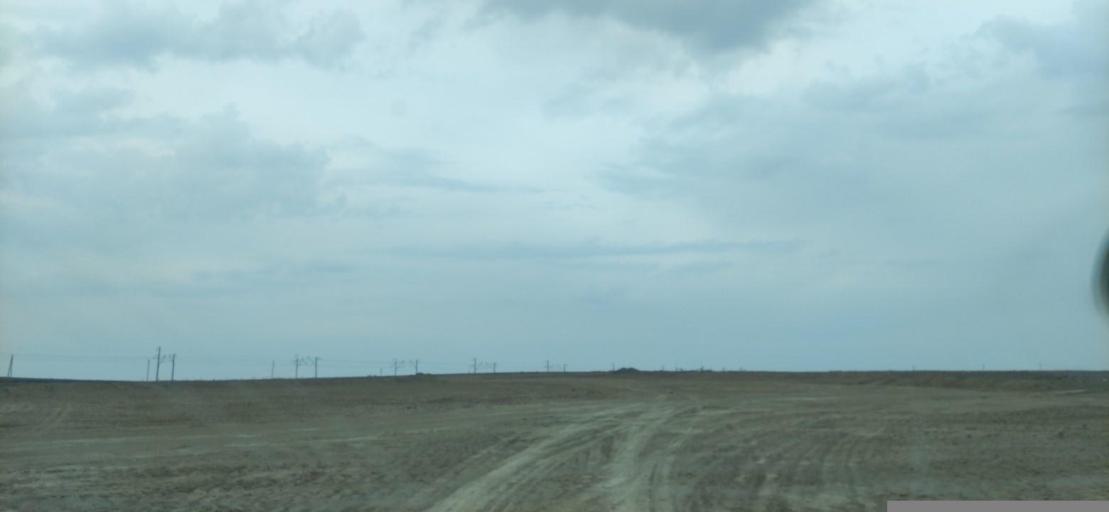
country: KZ
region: Qaraghandy
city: Saryshaghan
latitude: 46.0925
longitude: 73.6056
